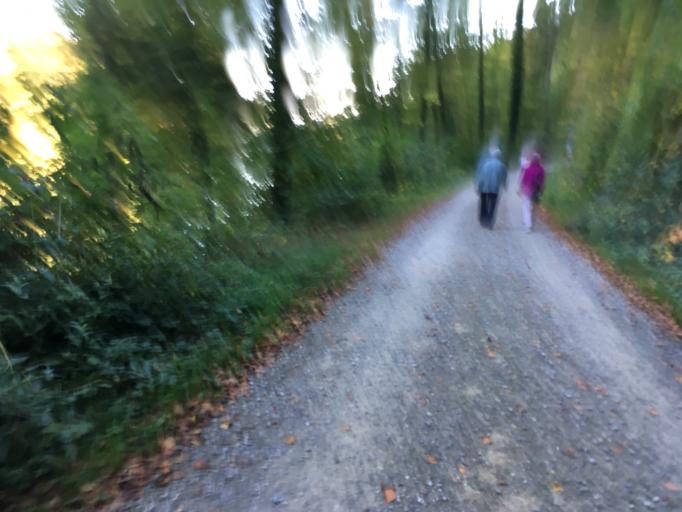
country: CH
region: Zurich
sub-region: Bezirk Buelach
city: Seglingen
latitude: 47.5574
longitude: 8.5491
